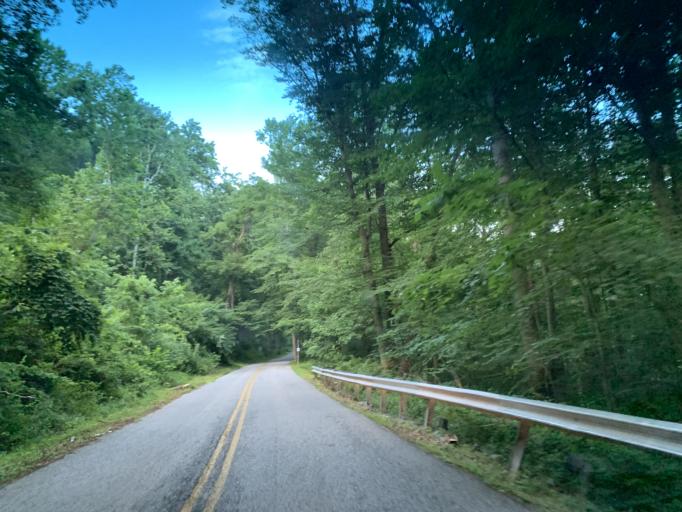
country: US
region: Maryland
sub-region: Harford County
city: Aberdeen
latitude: 39.5333
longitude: -76.1589
